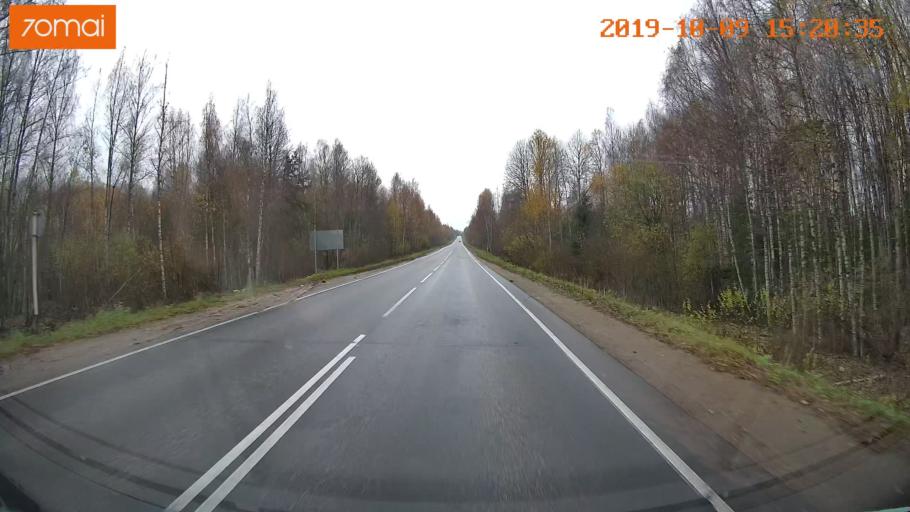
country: RU
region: Kostroma
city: Susanino
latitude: 58.0629
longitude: 41.5353
